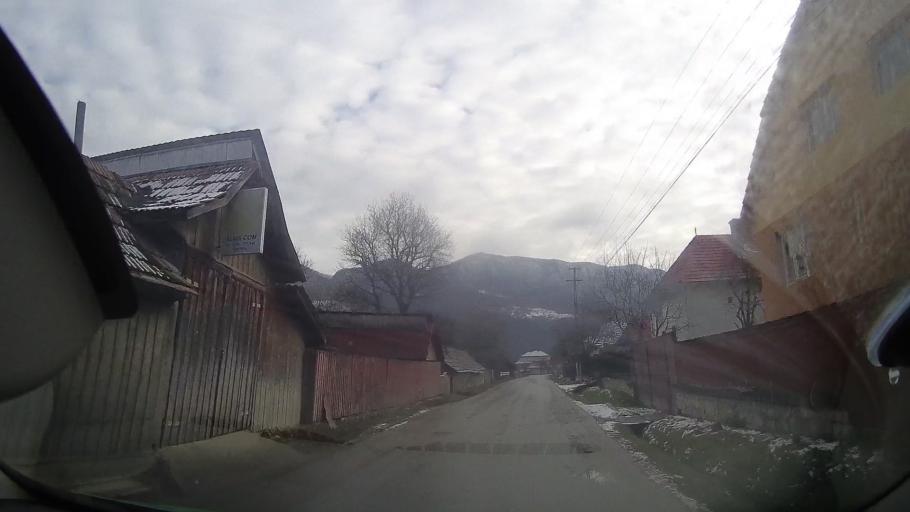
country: RO
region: Alba
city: Salciua de Sus
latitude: 46.4291
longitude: 23.4417
